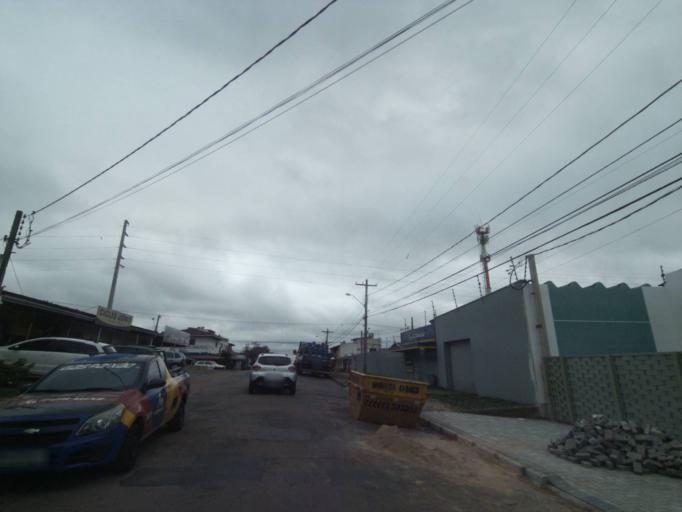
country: BR
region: Parana
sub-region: Curitiba
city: Curitiba
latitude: -25.5179
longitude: -49.3038
